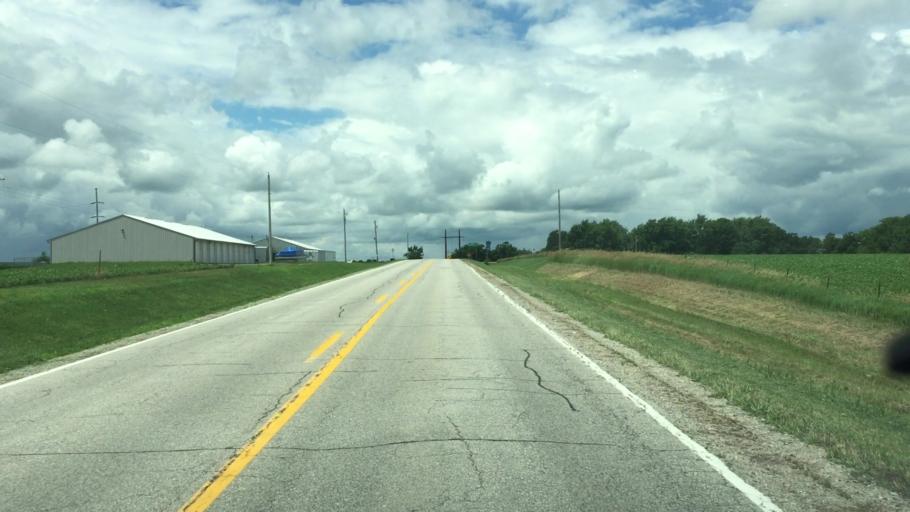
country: US
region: Iowa
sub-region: Jasper County
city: Monroe
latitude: 41.5735
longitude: -93.0938
